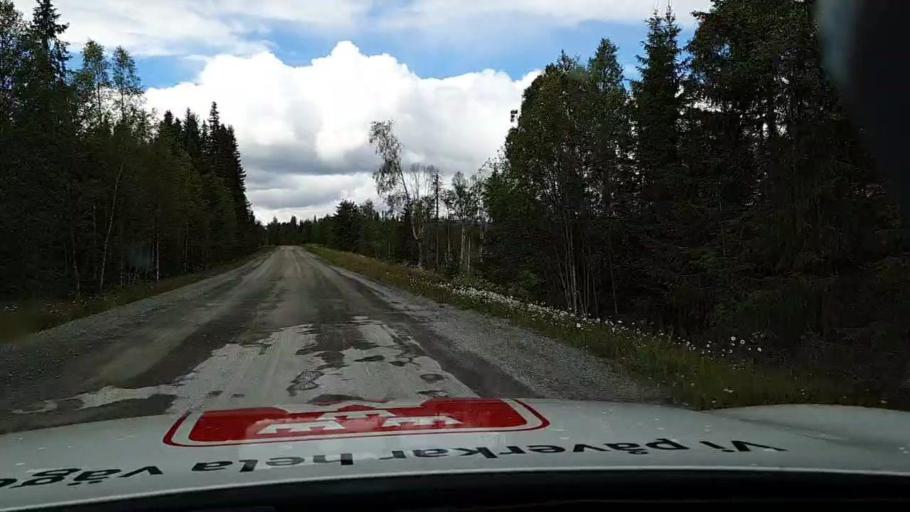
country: SE
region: Jaemtland
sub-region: Krokoms Kommun
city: Valla
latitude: 63.6893
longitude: 13.6740
